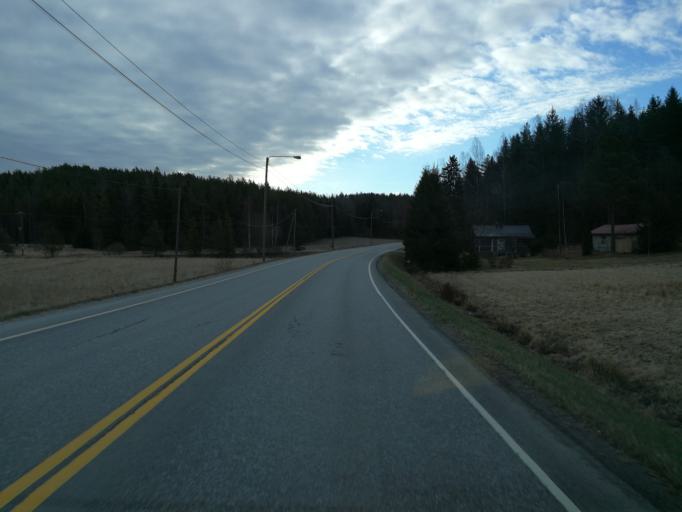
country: FI
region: Varsinais-Suomi
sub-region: Turku
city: Paimio
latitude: 60.4317
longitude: 22.6073
